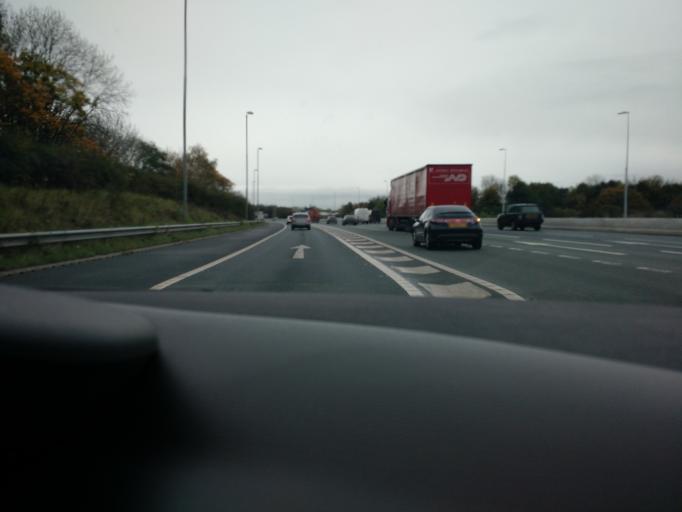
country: GB
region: England
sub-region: Lancashire
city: Goosnargh
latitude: 53.8020
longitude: -2.6921
